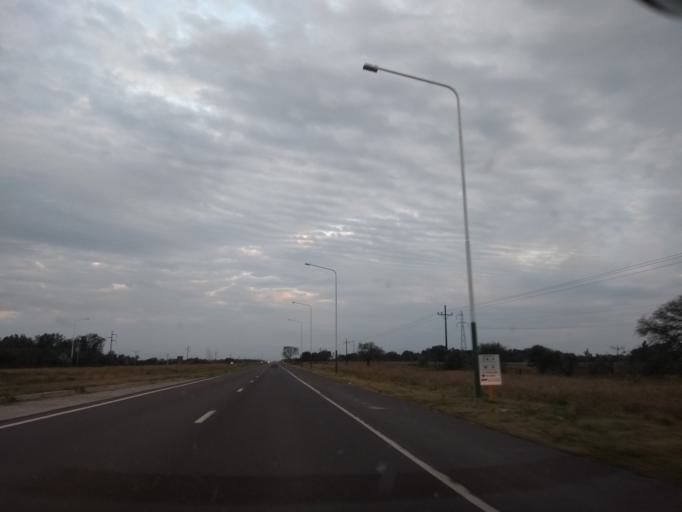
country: AR
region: Chaco
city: Puerto Tirol
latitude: -27.2706
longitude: -59.1442
